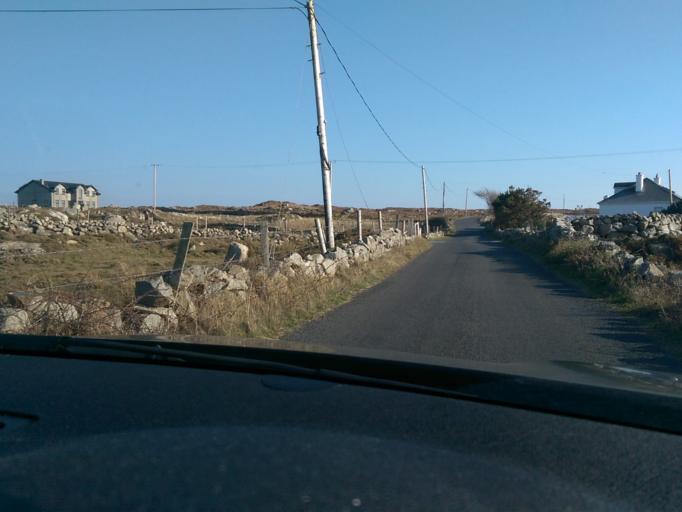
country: IE
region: Connaught
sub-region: County Galway
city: Clifden
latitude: 53.3548
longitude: -9.8737
